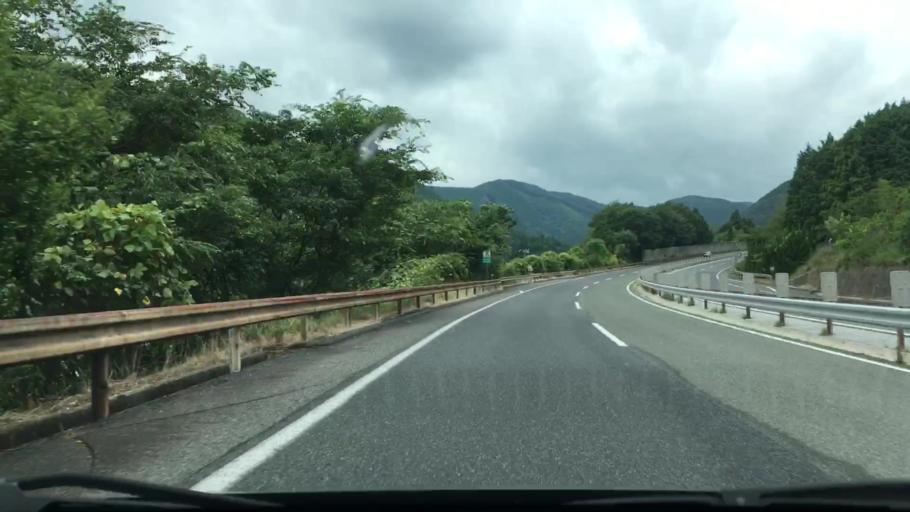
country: JP
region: Okayama
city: Niimi
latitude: 34.9840
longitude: 133.3808
